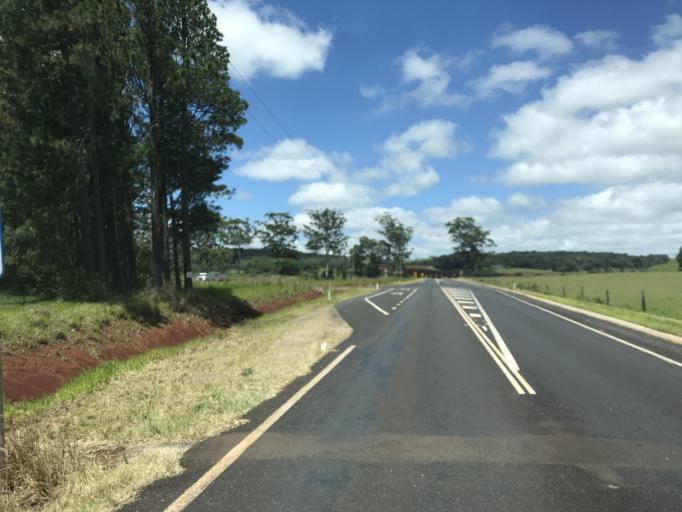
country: AU
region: Queensland
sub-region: Tablelands
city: Ravenshoe
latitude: -17.5098
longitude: 145.4547
